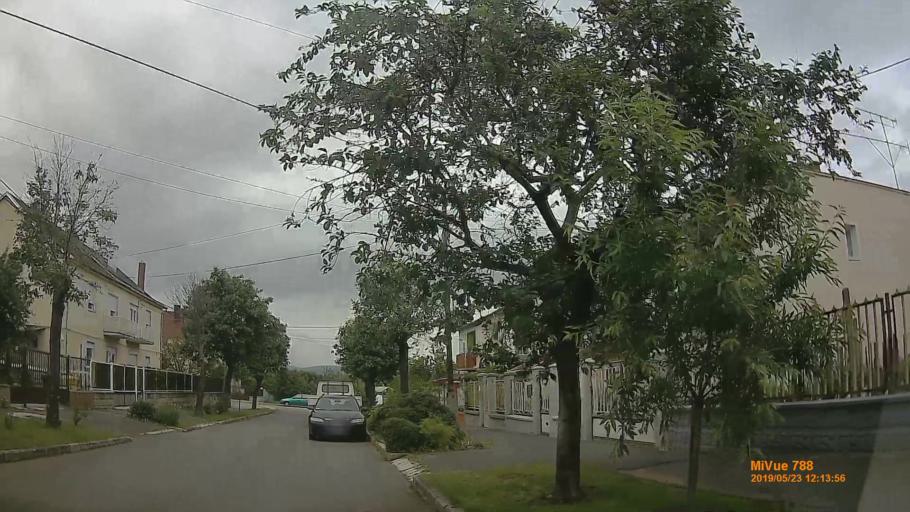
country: HU
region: Veszprem
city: Veszprem
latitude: 47.1054
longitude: 17.8951
